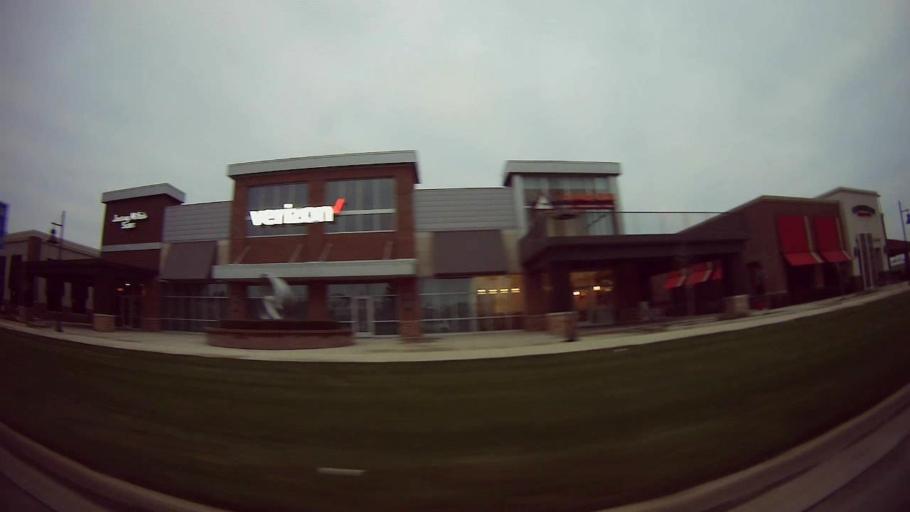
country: US
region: Michigan
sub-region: Oakland County
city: Clawson
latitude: 42.5622
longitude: -83.1616
